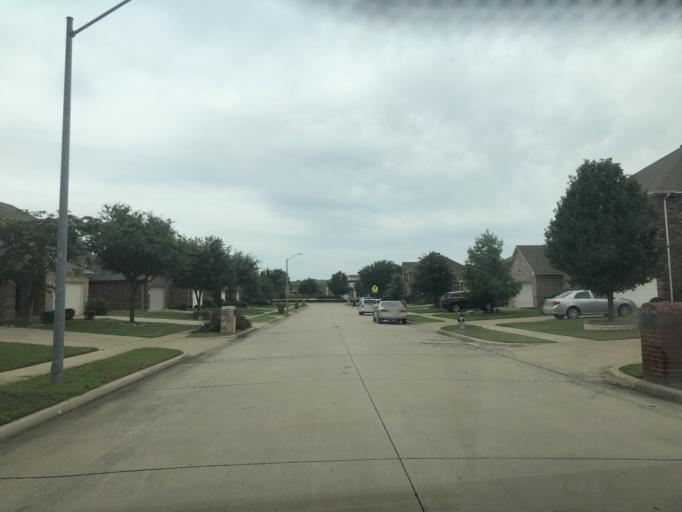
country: US
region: Texas
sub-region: Dallas County
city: Irving
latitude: 32.8007
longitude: -96.9901
